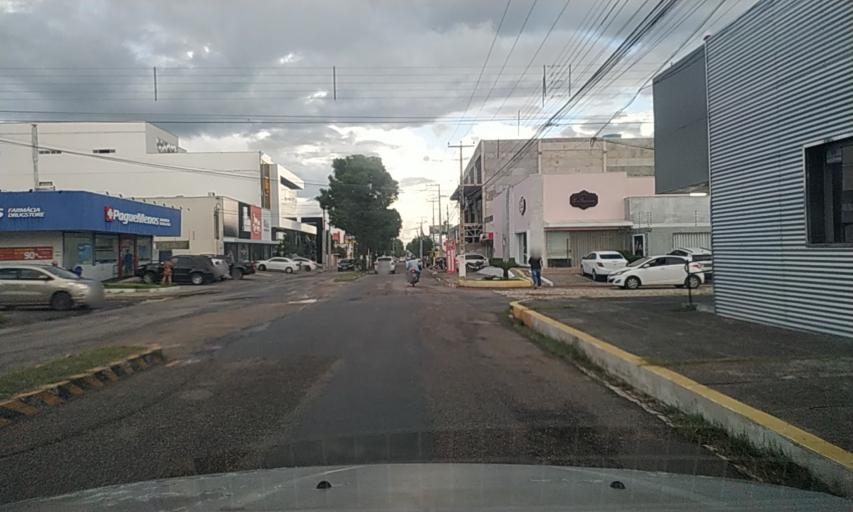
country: BR
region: Rio Grande do Norte
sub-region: Mossoro
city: Mossoro
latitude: -5.1832
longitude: -37.3587
